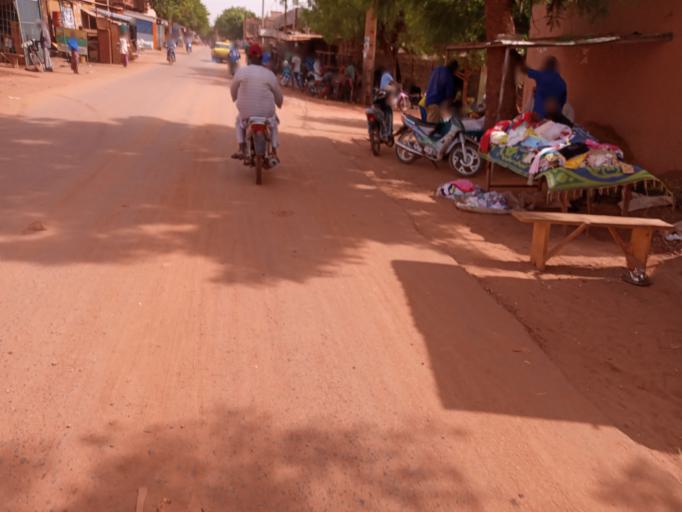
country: ML
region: Bamako
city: Bamako
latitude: 12.6083
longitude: -7.9523
